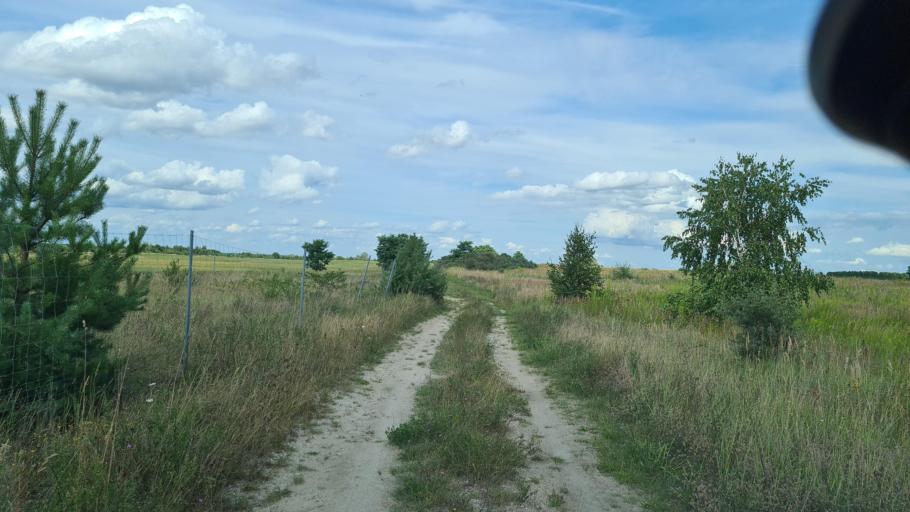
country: DE
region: Brandenburg
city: Spremberg
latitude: 51.5955
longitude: 14.3117
